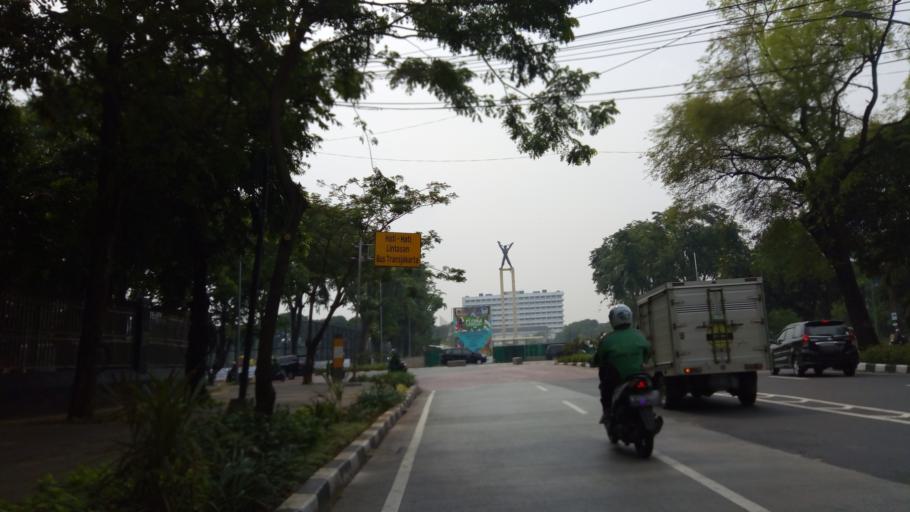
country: ID
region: Jakarta Raya
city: Jakarta
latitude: -6.1713
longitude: 106.8330
